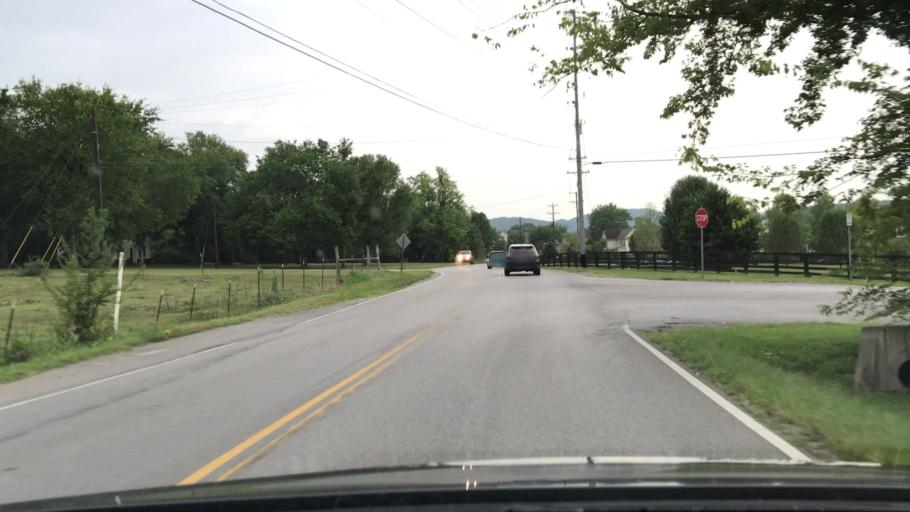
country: US
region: Tennessee
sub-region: Williamson County
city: Nolensville
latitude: 35.9486
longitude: -86.6708
